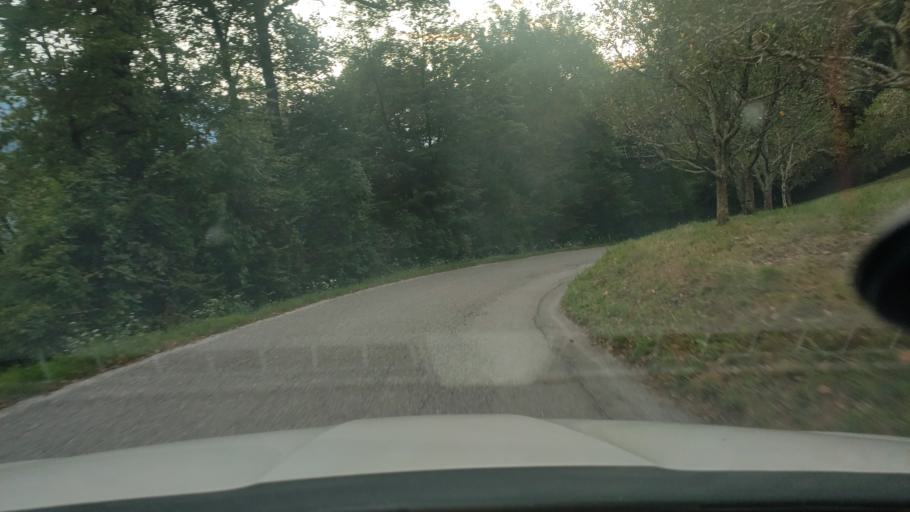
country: IT
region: Friuli Venezia Giulia
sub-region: Provincia di Udine
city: Cras
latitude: 46.2162
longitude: 13.6380
